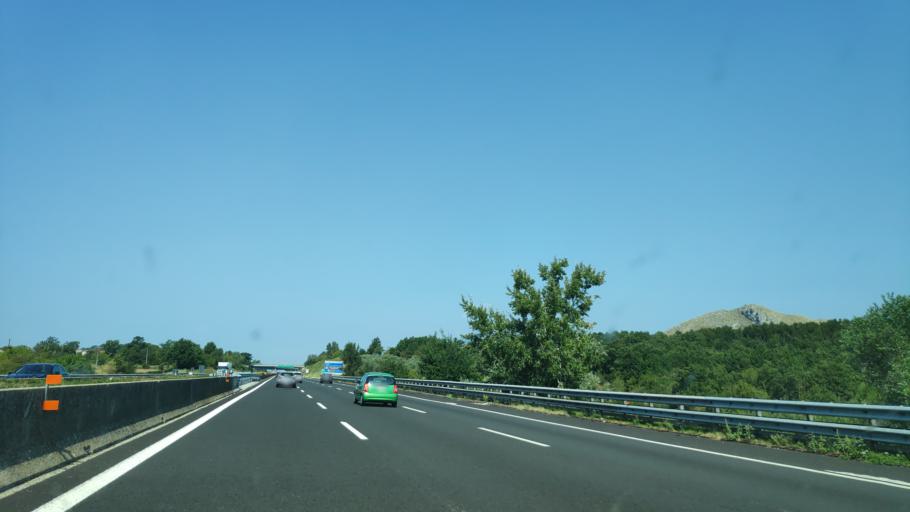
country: IT
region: Campania
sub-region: Provincia di Caserta
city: Bivio Mortola
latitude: 41.4290
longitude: 13.9076
